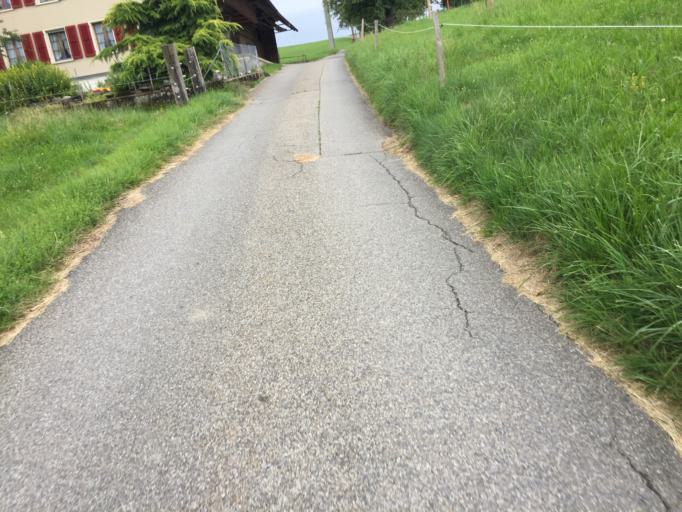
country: CH
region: Bern
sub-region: Bern-Mittelland District
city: Biglen
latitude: 46.9063
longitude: 7.6207
